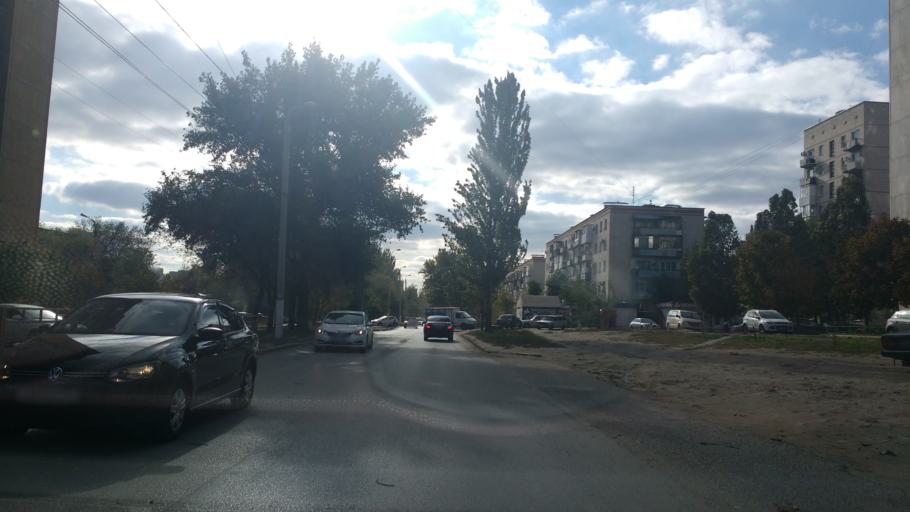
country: RU
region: Volgograd
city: Vodstroy
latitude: 48.7782
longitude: 44.5666
